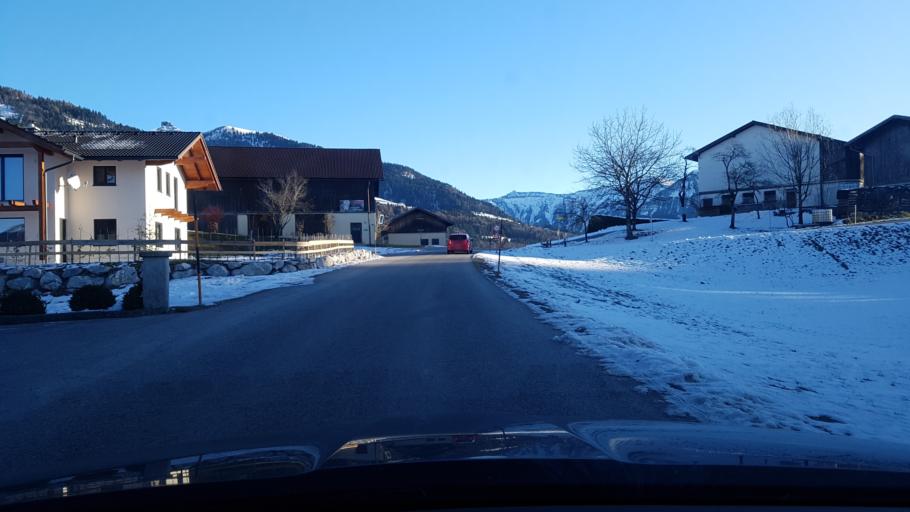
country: AT
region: Salzburg
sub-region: Politischer Bezirk Hallein
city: Kuchl
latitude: 47.6567
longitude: 13.1914
